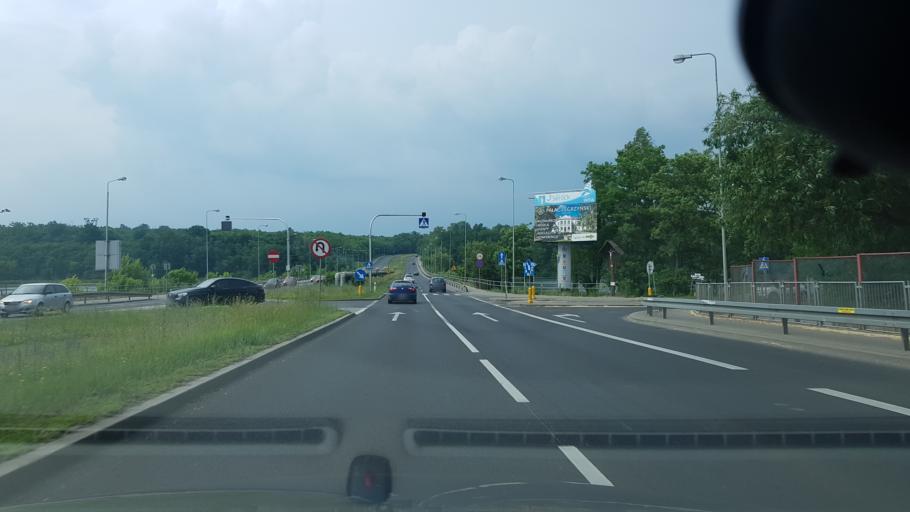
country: PL
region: Masovian Voivodeship
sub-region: Powiat legionowski
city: Nieporet
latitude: 52.4593
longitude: 21.0188
